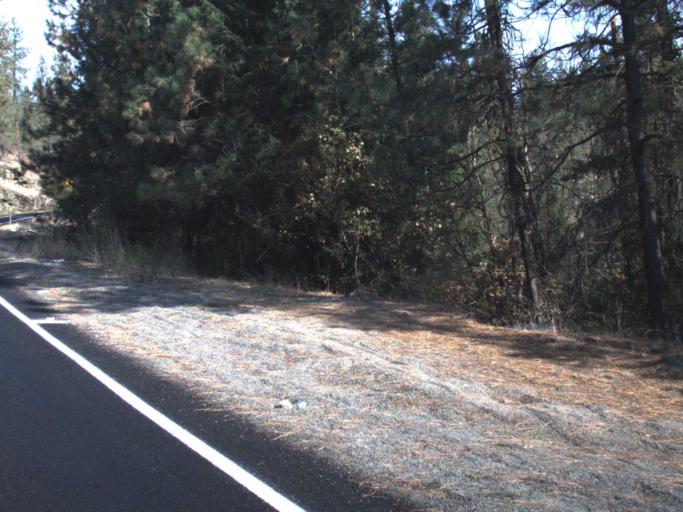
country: US
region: Washington
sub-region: Spokane County
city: Deer Park
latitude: 47.8776
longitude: -117.7042
